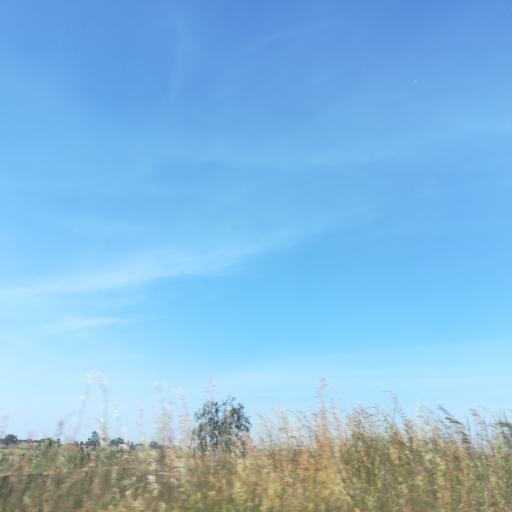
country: NG
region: Plateau
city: Bukuru
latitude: 9.7700
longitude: 8.8875
